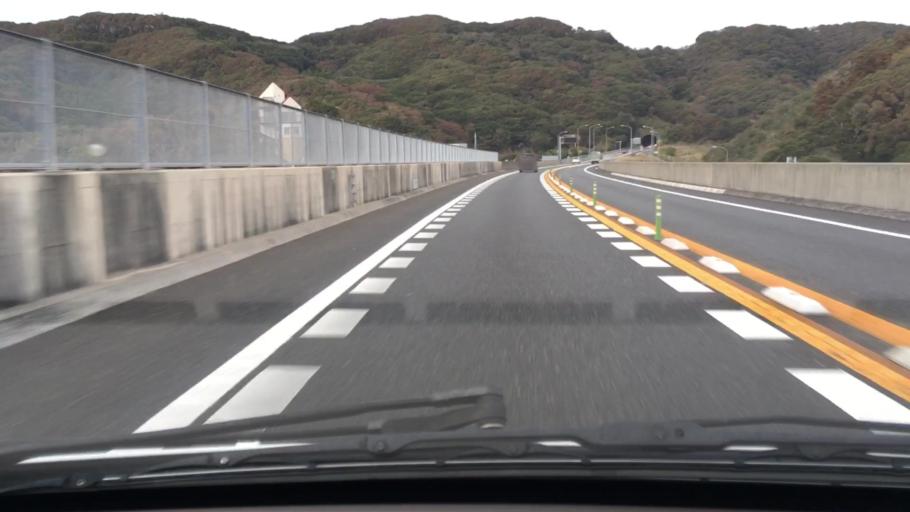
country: JP
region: Chiba
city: Futtsu
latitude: 35.1692
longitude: 139.8303
